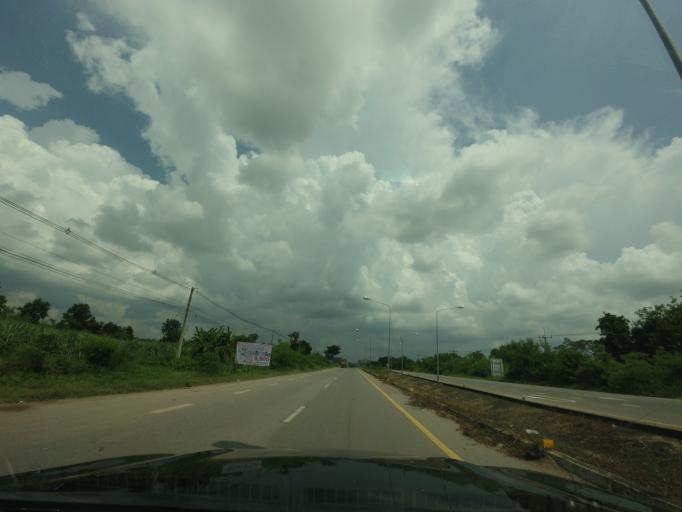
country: TH
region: Khon Kaen
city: Nong Ruea
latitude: 16.4938
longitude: 102.4062
